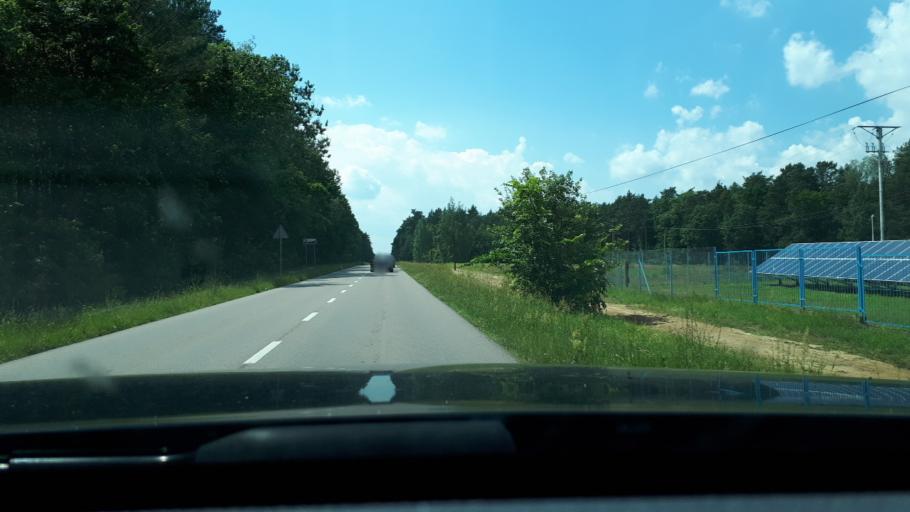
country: PL
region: Podlasie
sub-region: Powiat bialostocki
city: Choroszcz
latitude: 53.1314
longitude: 23.0436
